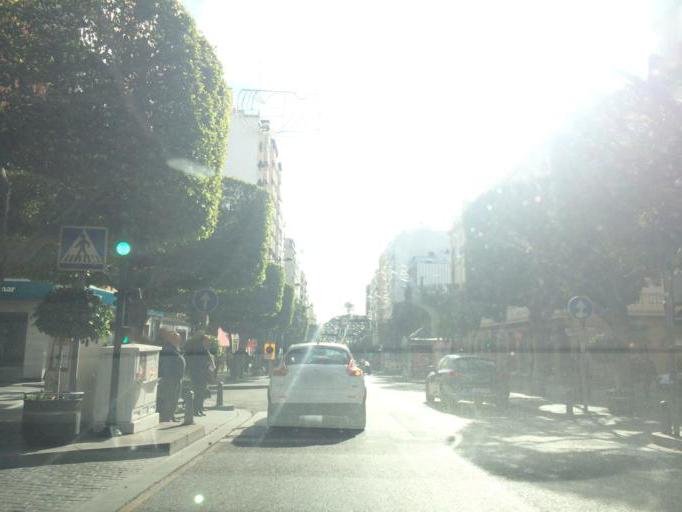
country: ES
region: Andalusia
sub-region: Provincia de Almeria
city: Almeria
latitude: 36.8398
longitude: -2.4636
